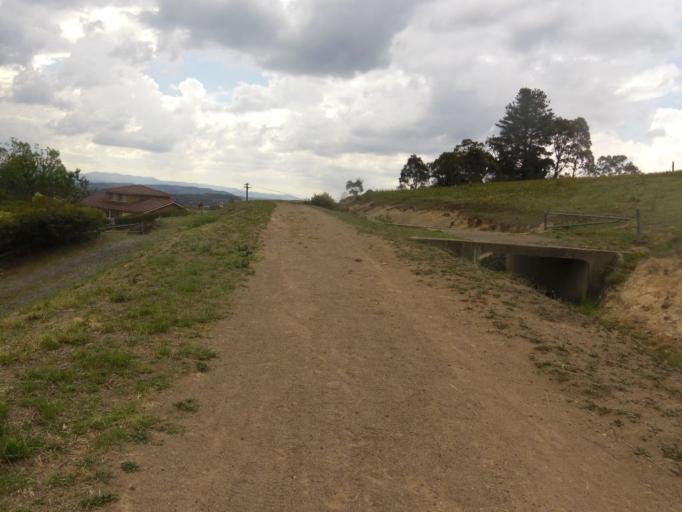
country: AU
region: Australian Capital Territory
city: Forrest
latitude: -35.3600
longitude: 149.1130
